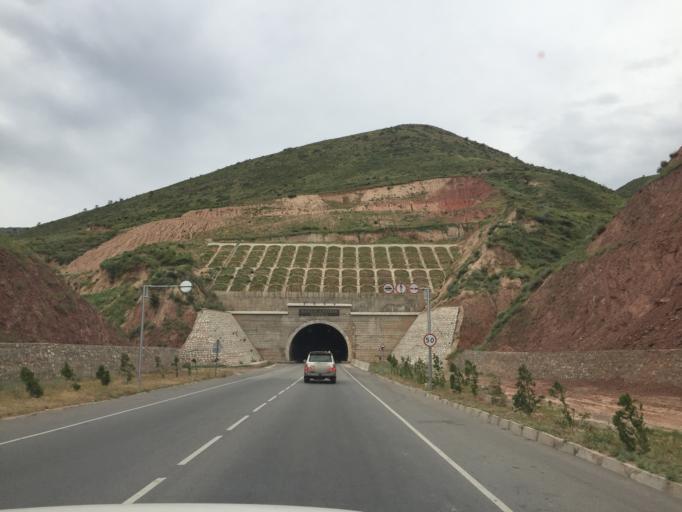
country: TJ
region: Republican Subordination
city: Vahdat
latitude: 38.4876
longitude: 69.1761
